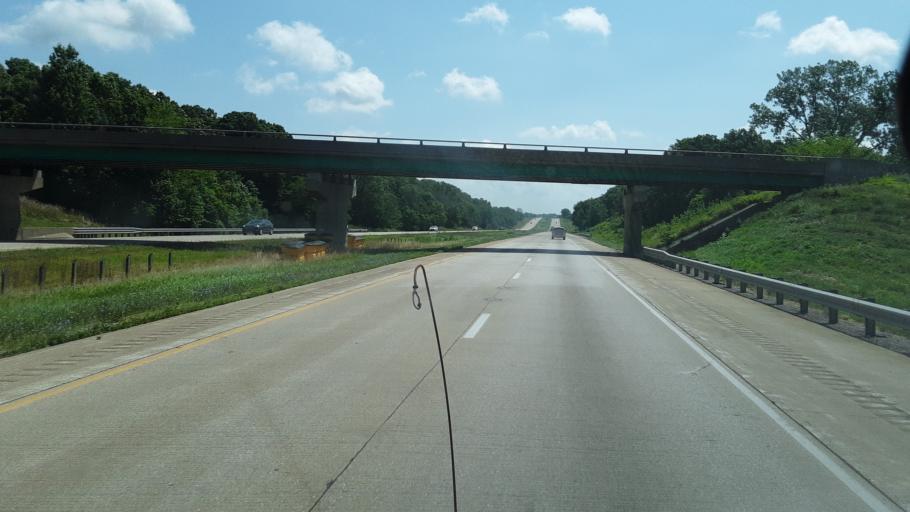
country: US
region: Illinois
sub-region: Clark County
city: Marshall
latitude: 39.4217
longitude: -87.6544
